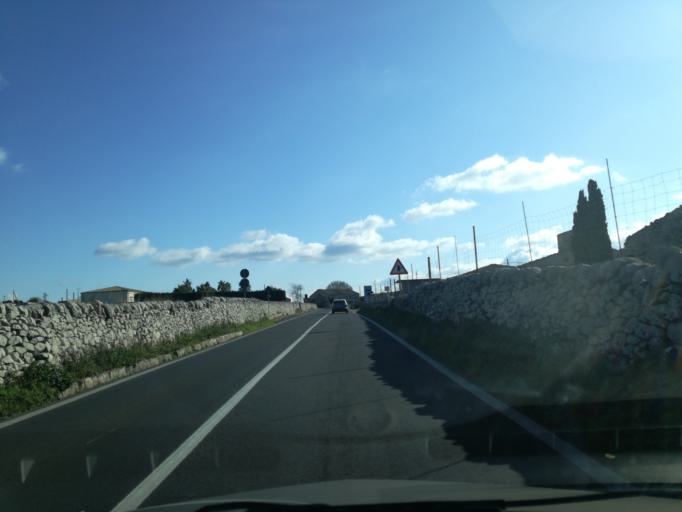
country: IT
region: Sicily
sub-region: Ragusa
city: Comiso
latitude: 36.9409
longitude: 14.6432
